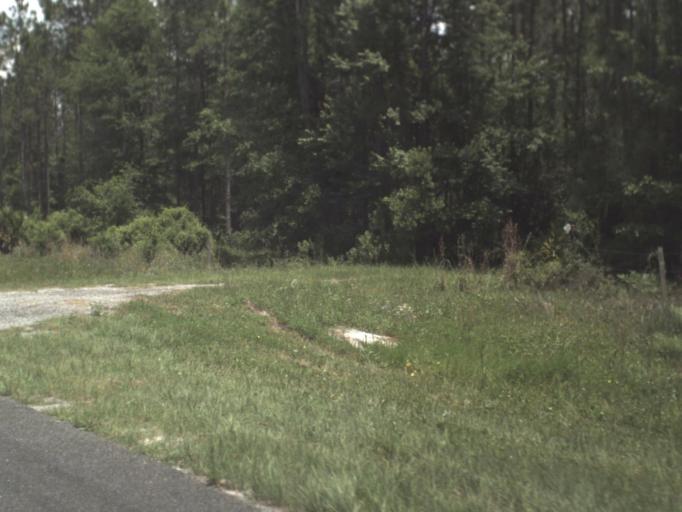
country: US
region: Florida
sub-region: Union County
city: Lake Butler
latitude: 30.0662
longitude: -82.4317
